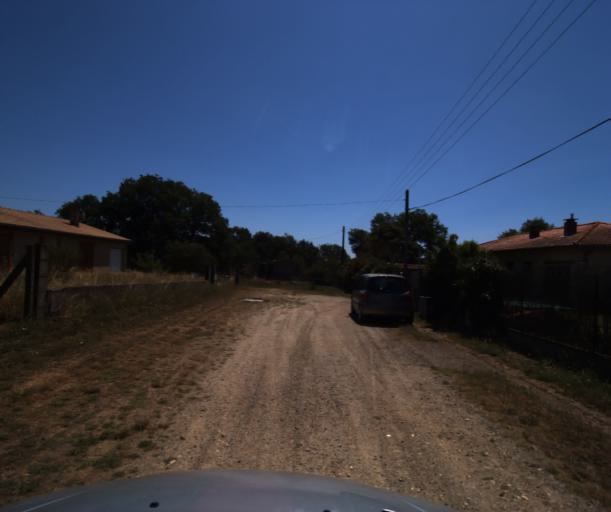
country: FR
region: Midi-Pyrenees
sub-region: Departement de la Haute-Garonne
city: Muret
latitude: 43.4540
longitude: 1.3411
